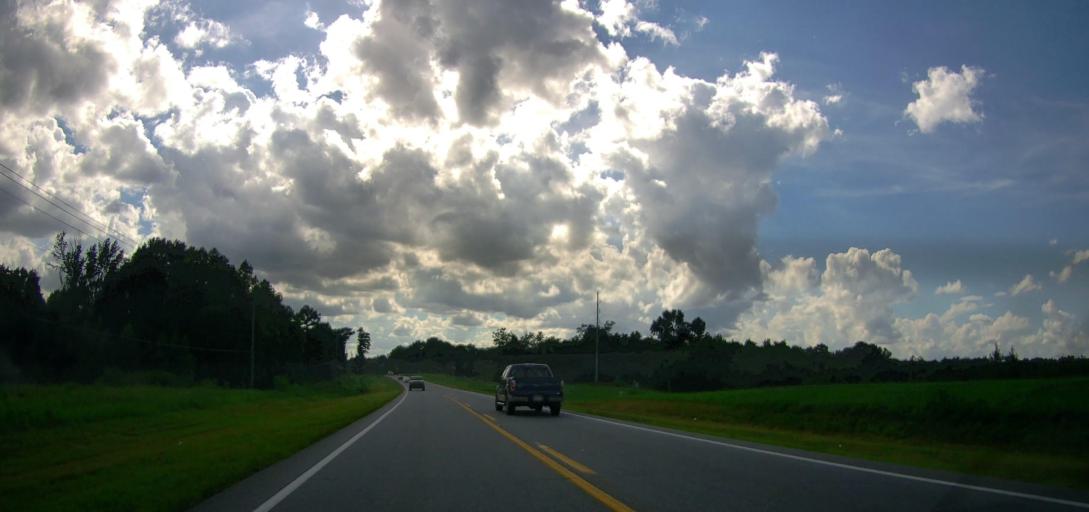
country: US
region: Alabama
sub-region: Russell County
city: Ladonia
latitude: 32.4625
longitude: -85.1595
